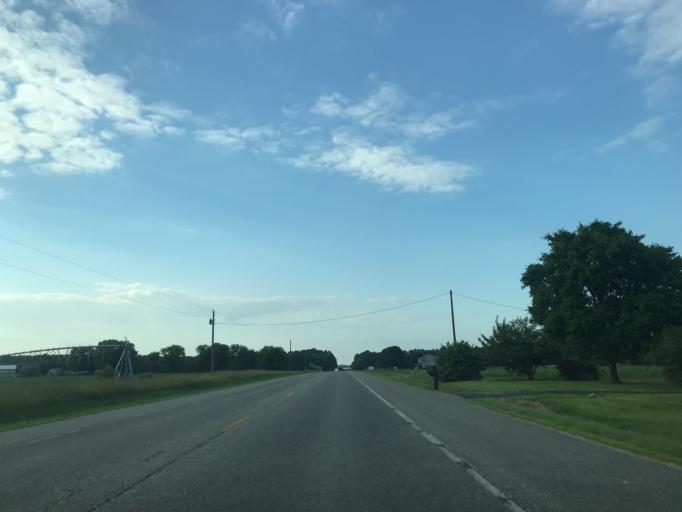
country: US
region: Maryland
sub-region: Caroline County
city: Federalsburg
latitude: 38.7826
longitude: -75.7876
